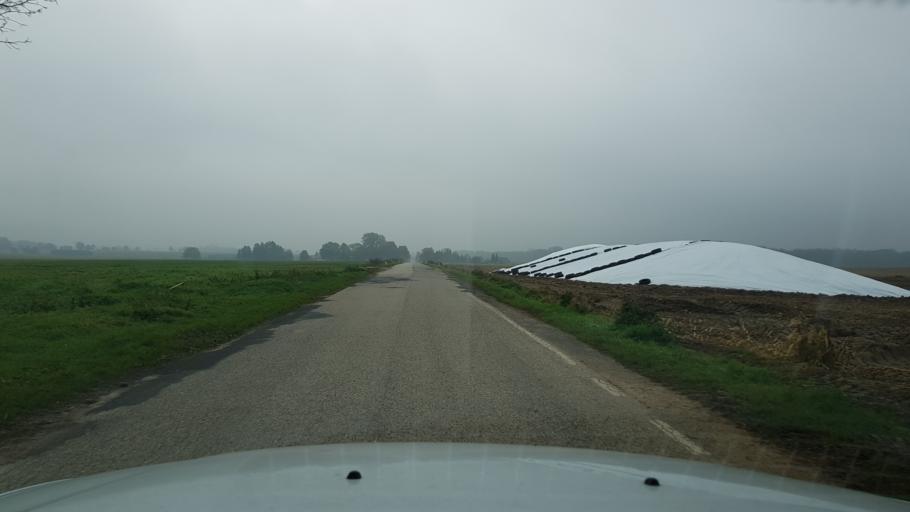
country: PL
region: West Pomeranian Voivodeship
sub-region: Powiat stargardzki
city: Dolice
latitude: 53.1678
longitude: 15.2240
